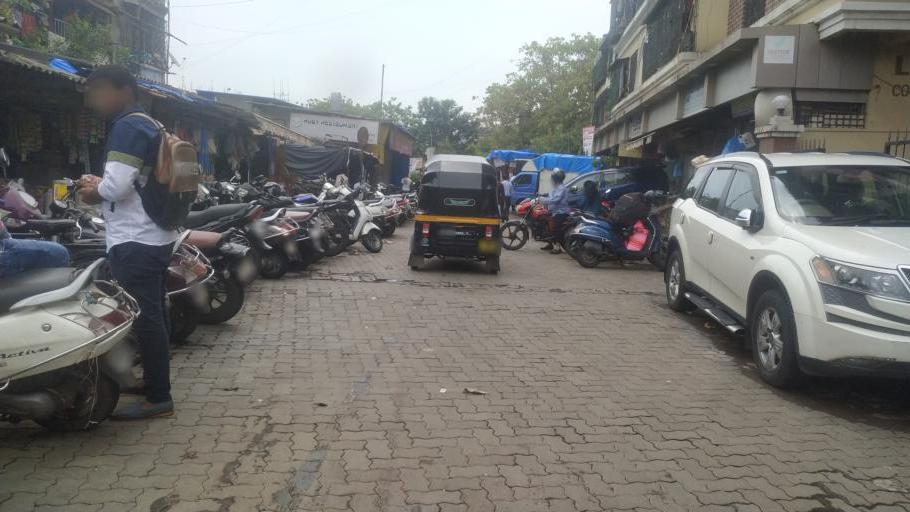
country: IN
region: Maharashtra
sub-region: Mumbai Suburban
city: Mumbai
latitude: 19.0572
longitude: 72.8389
